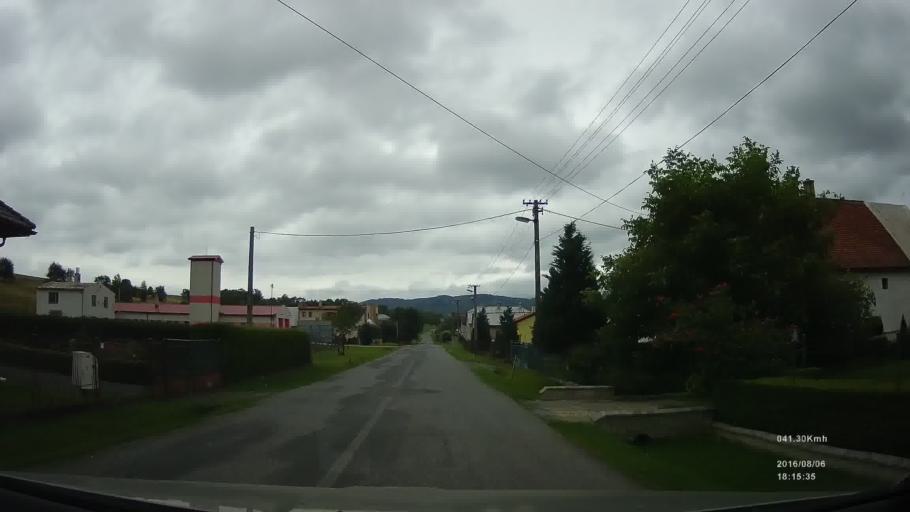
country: SK
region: Presovsky
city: Svidnik
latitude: 49.3442
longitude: 21.5955
